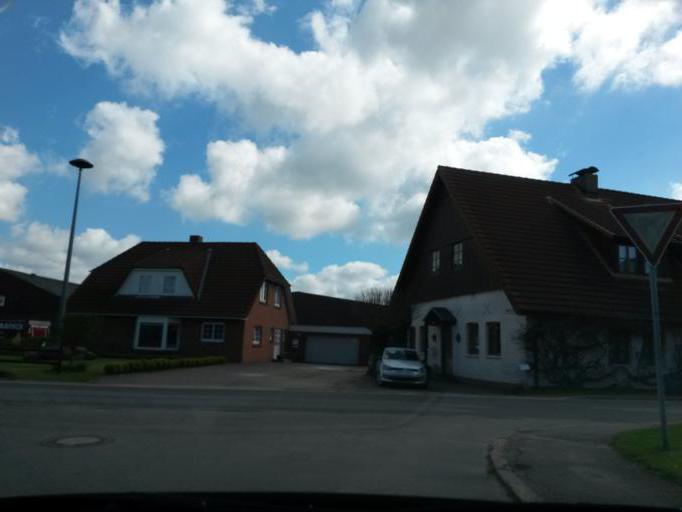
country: DE
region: Schleswig-Holstein
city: Haseldorf
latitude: 53.6428
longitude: 9.5737
